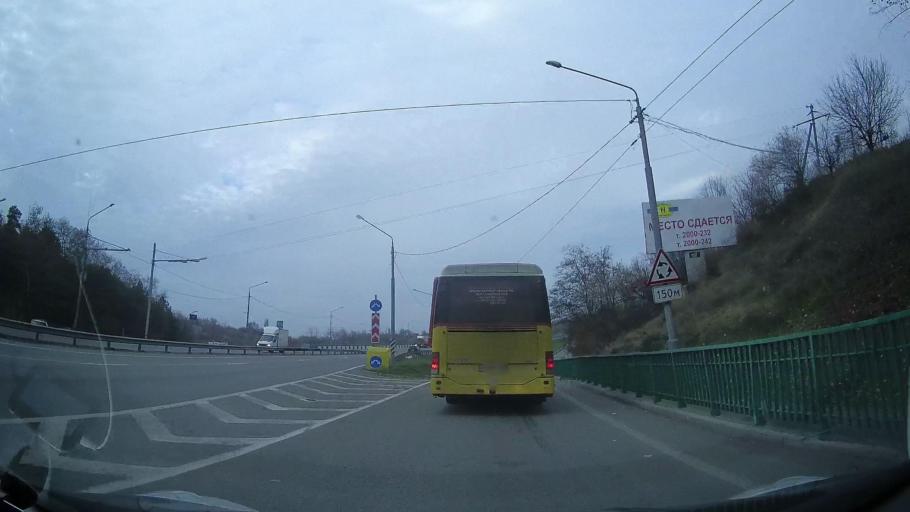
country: RU
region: Rostov
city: Aksay
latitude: 47.2465
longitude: 39.8468
